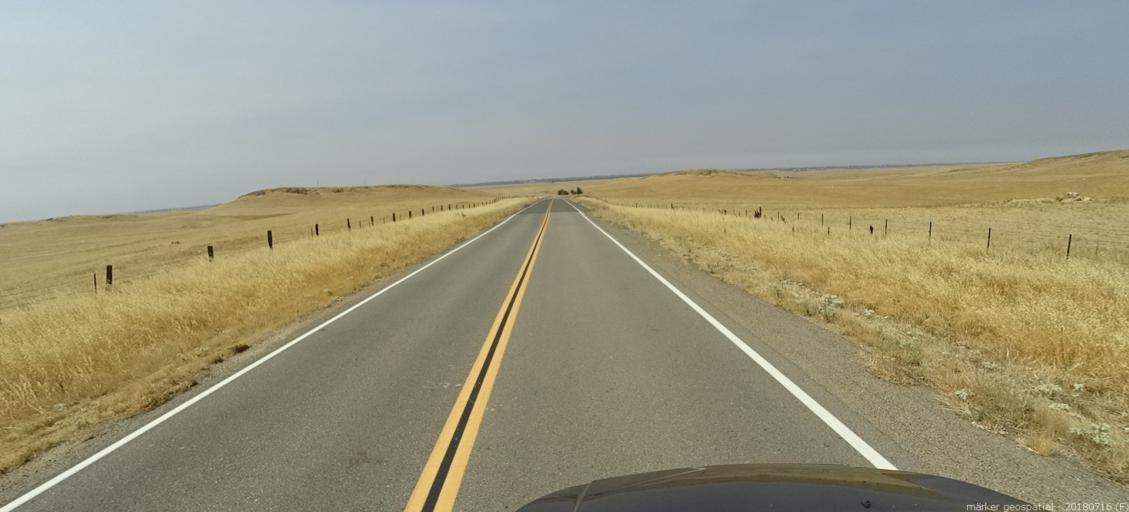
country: US
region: California
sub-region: Madera County
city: Bonadelle Ranchos-Madera Ranchos
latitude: 37.0940
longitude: -119.9503
